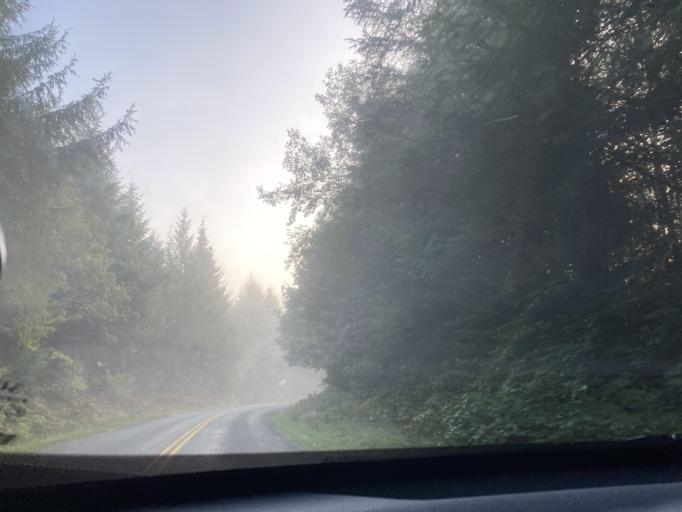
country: US
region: Washington
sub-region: Clallam County
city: Forks
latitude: 47.8091
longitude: -124.0908
